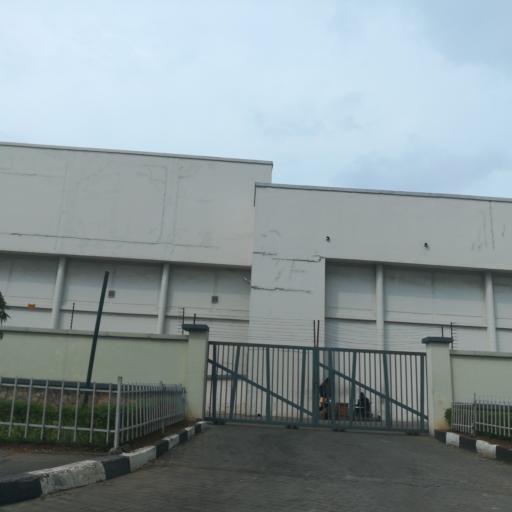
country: NG
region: Lagos
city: Ikeja
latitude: 6.6146
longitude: 3.3590
